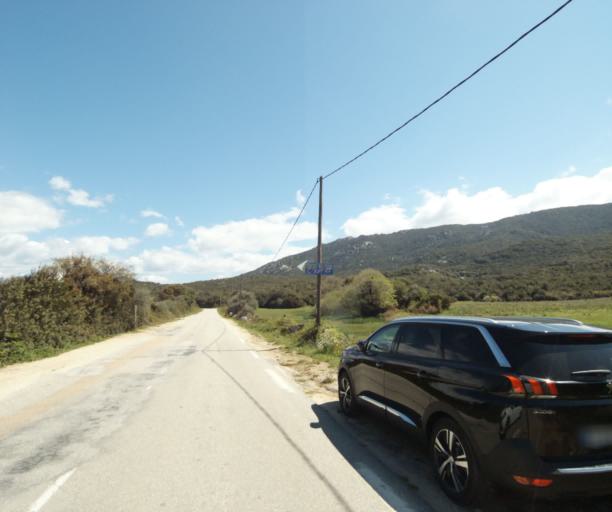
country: FR
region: Corsica
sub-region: Departement de la Corse-du-Sud
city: Propriano
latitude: 41.6449
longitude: 8.8696
